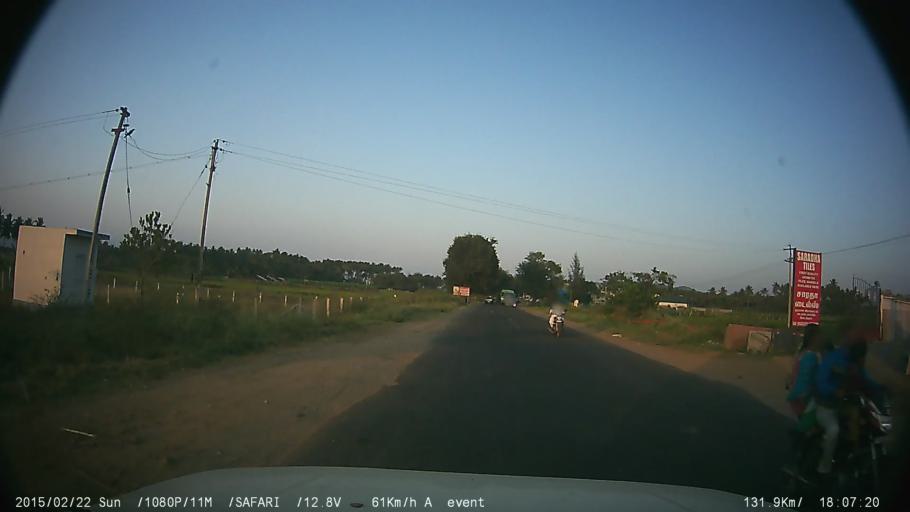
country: IN
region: Tamil Nadu
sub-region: Theni
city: Chinnamanur
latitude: 9.8326
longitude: 77.3740
